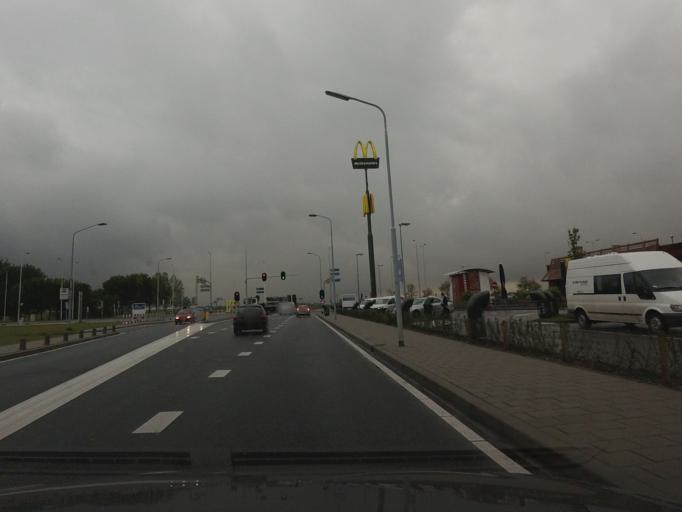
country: NL
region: North Holland
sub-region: Gemeente Haarlemmermeer
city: Hoofddorp
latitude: 52.2895
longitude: 4.7243
